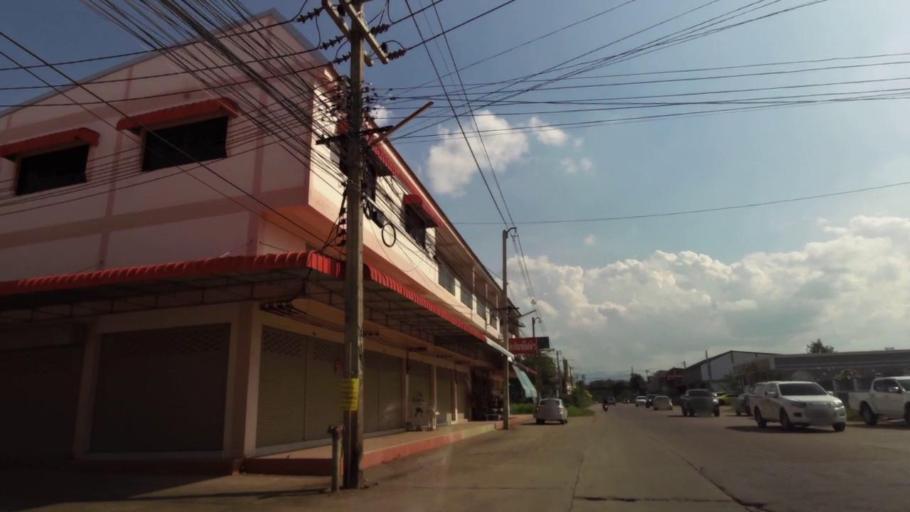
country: TH
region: Phrae
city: Phrae
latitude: 18.1206
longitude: 100.1544
